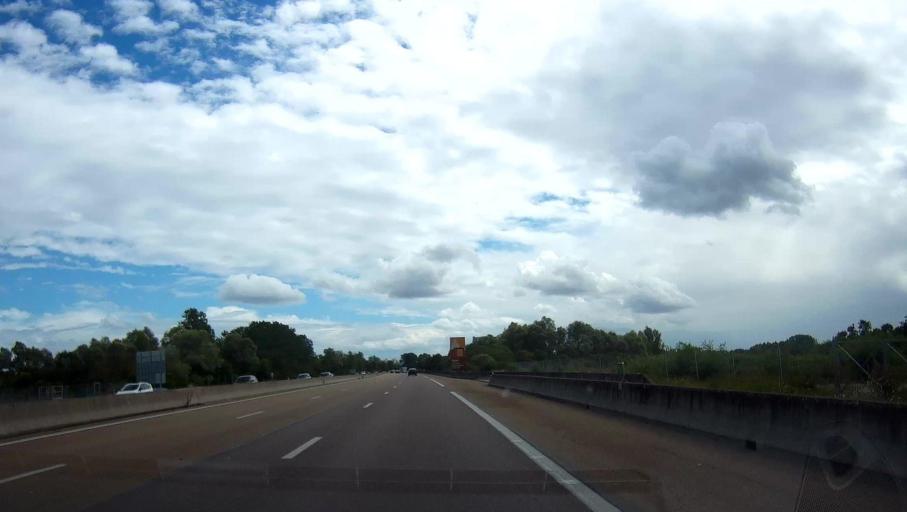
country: FR
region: Bourgogne
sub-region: Departement de la Cote-d'Or
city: Saint-Julien
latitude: 47.4119
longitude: 5.1778
